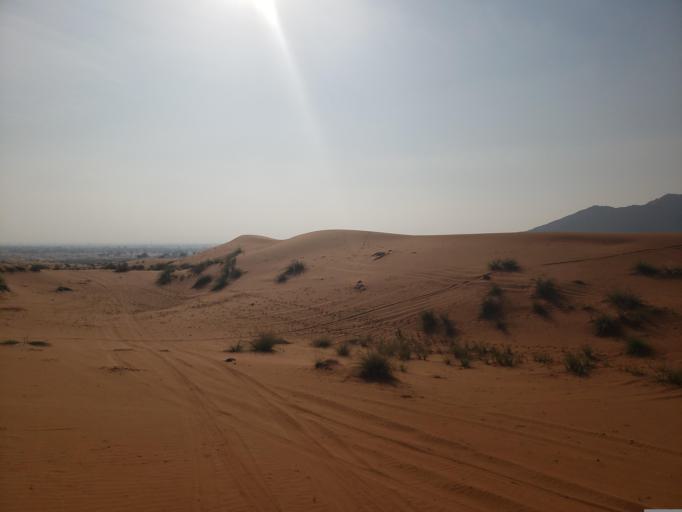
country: AE
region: Ash Shariqah
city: Adh Dhayd
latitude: 25.1391
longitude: 55.8418
